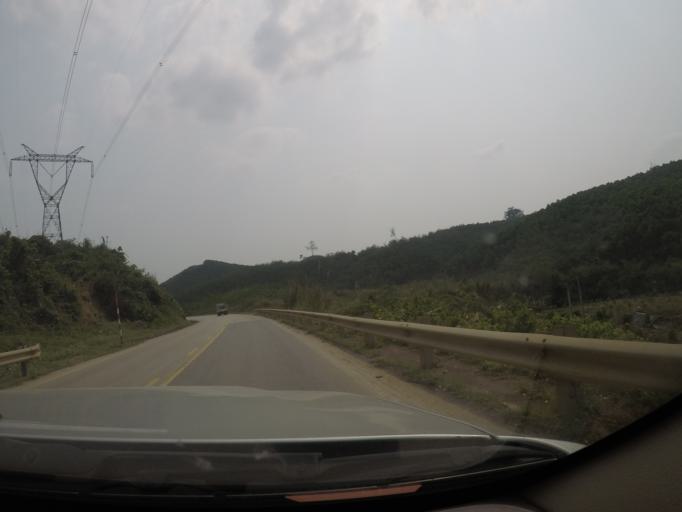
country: VN
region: Thanh Hoa
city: Thi Tran Yen Cat
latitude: 19.5055
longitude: 105.3910
